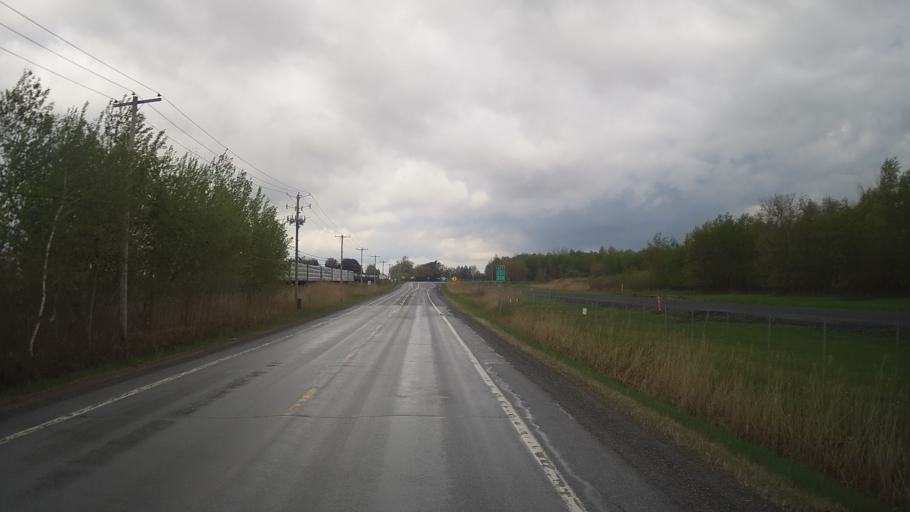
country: CA
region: Quebec
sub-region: Monteregie
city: Farnham
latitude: 45.2885
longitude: -73.0083
